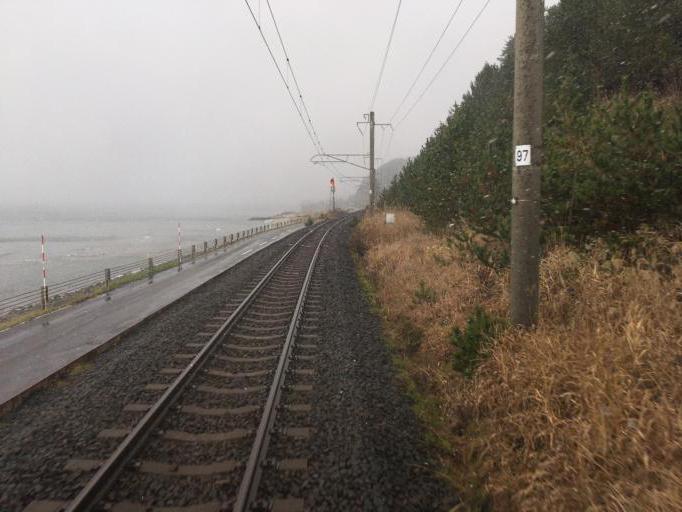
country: JP
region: Aomori
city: Aomori Shi
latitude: 41.0284
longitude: 140.6465
